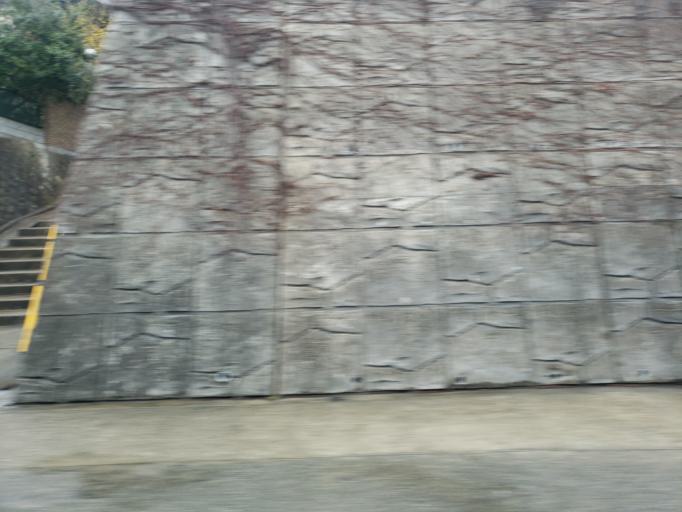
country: JP
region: Hyogo
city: Kobe
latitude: 34.6425
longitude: 135.1080
